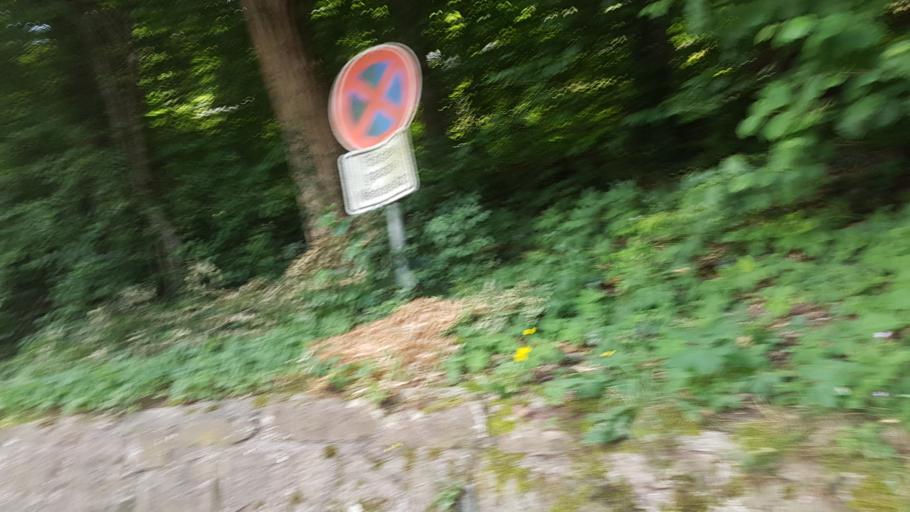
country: DE
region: Baden-Wuerttemberg
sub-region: Freiburg Region
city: Schramberg
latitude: 48.2289
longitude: 8.3978
